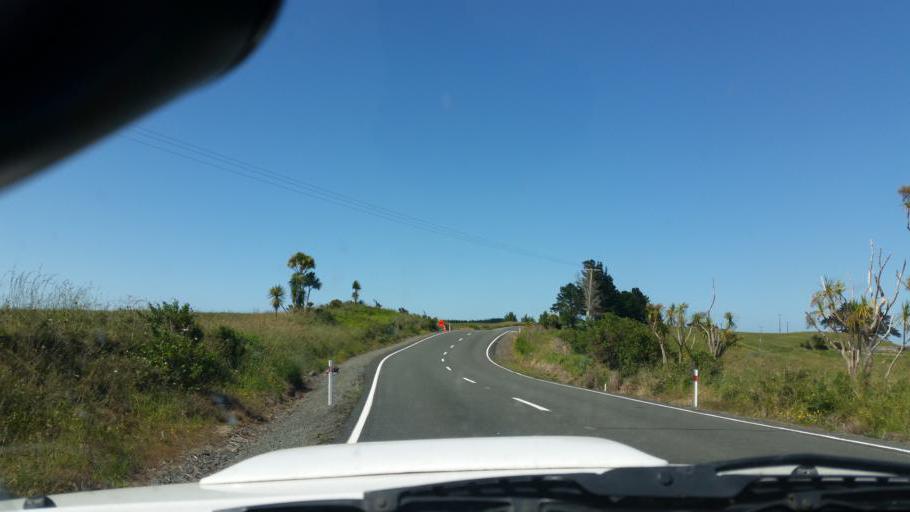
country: NZ
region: Auckland
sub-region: Auckland
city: Wellsford
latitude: -36.2211
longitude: 174.3800
